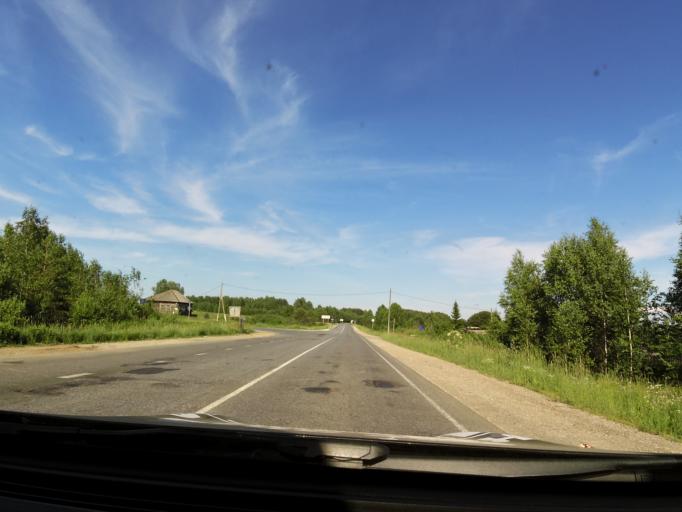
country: RU
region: Kirov
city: Belaya Kholunitsa
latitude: 58.8933
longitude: 50.8864
